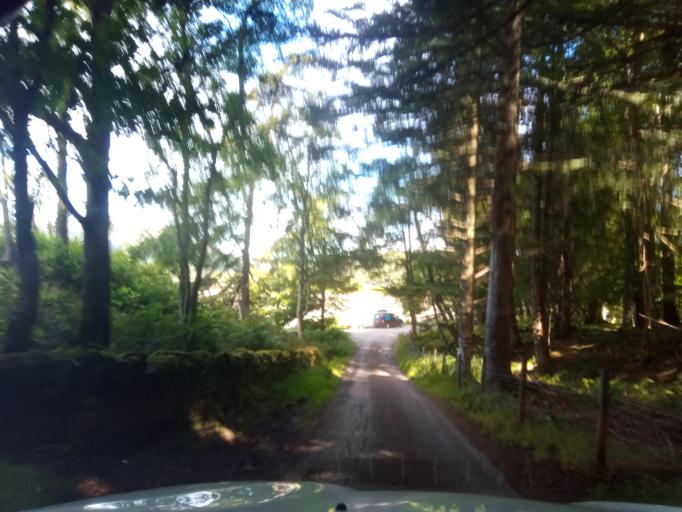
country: GB
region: Scotland
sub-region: Argyll and Bute
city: Isle Of Mull
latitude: 56.7801
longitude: -5.8255
